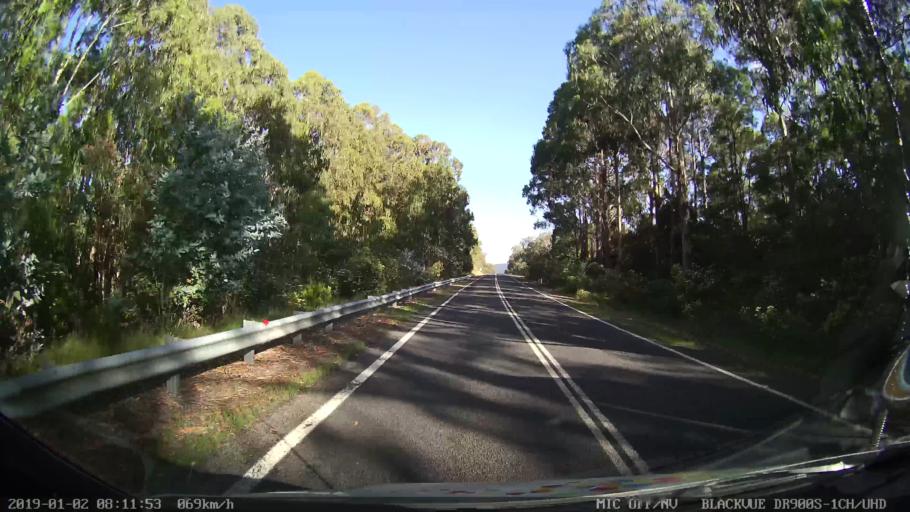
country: AU
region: New South Wales
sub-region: Tumut Shire
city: Tumut
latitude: -35.5927
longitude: 148.3527
